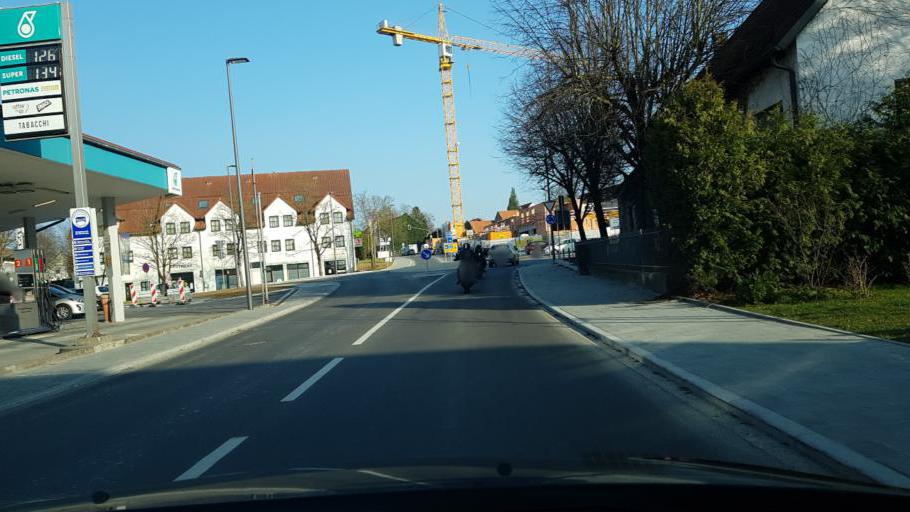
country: DE
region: Bavaria
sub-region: Upper Bavaria
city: Odelzhausen
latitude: 48.3097
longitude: 11.1934
